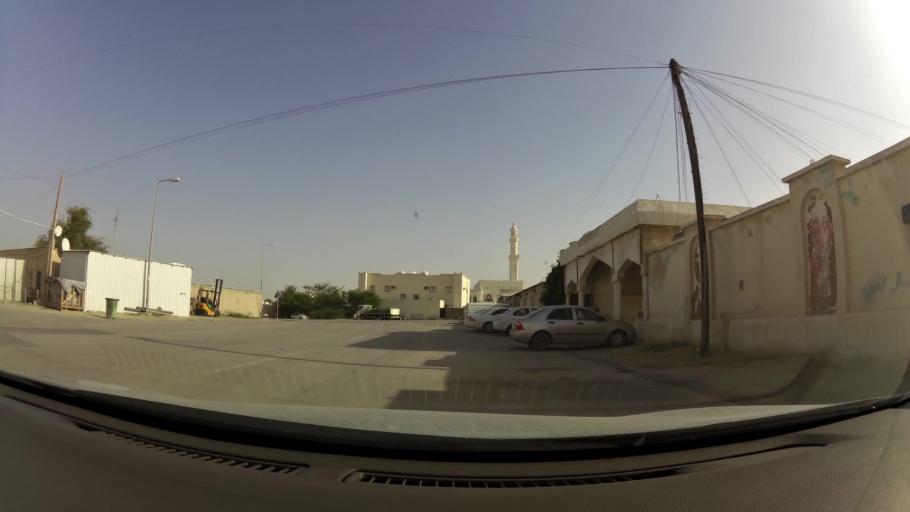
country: QA
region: Baladiyat ar Rayyan
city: Ar Rayyan
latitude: 25.3327
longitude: 51.4430
